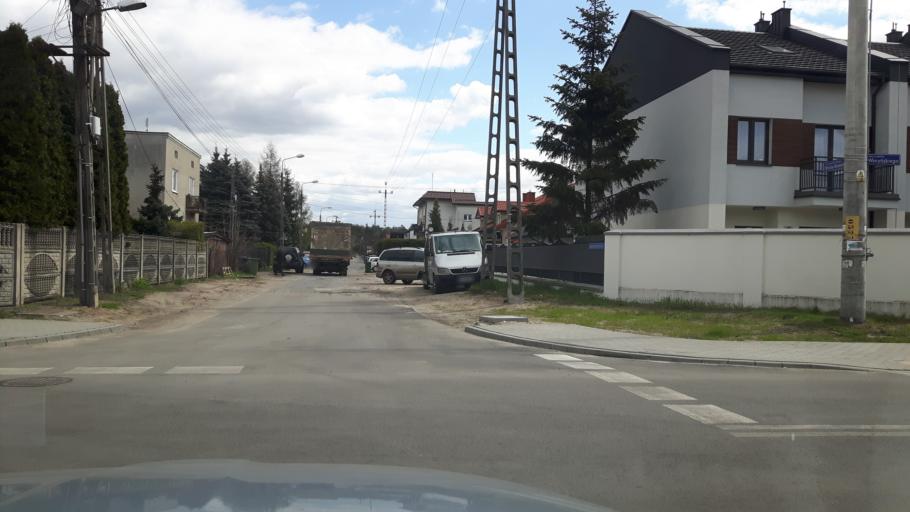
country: PL
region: Masovian Voivodeship
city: Zielonka
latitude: 52.2931
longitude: 21.1553
